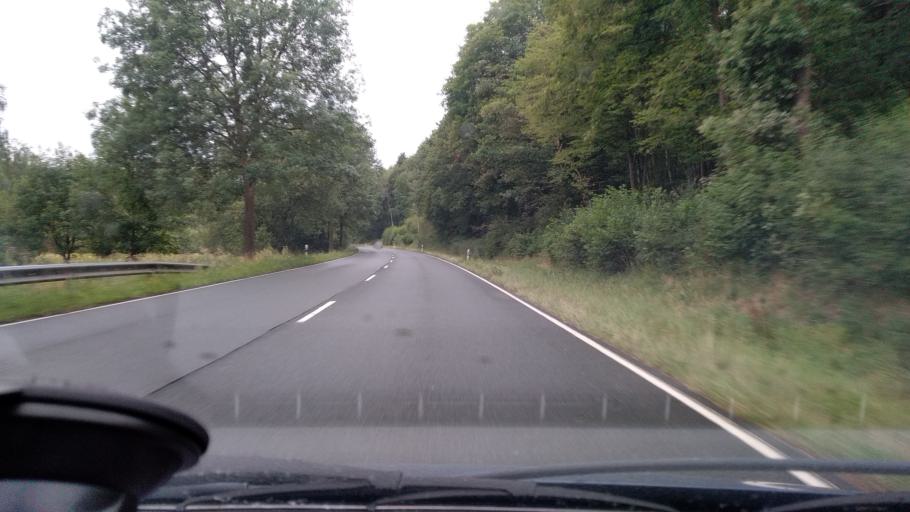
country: DE
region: North Rhine-Westphalia
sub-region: Regierungsbezirk Arnsberg
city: Burbach
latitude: 50.7557
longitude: 8.0999
